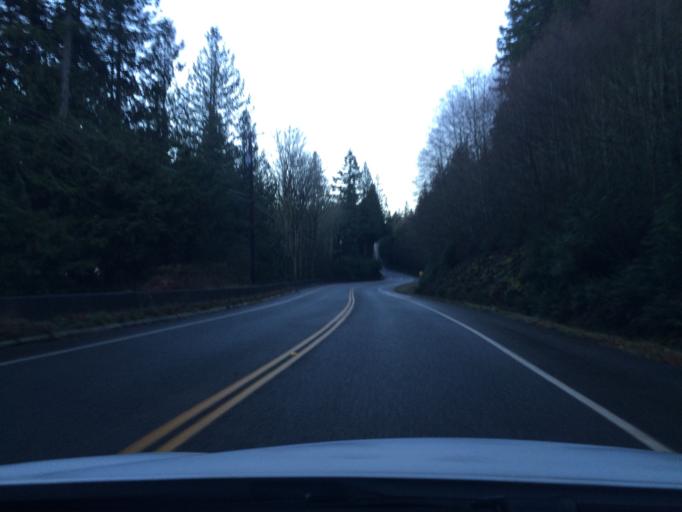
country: US
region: Washington
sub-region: Whatcom County
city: Sudden Valley
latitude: 48.7318
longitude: -122.3474
